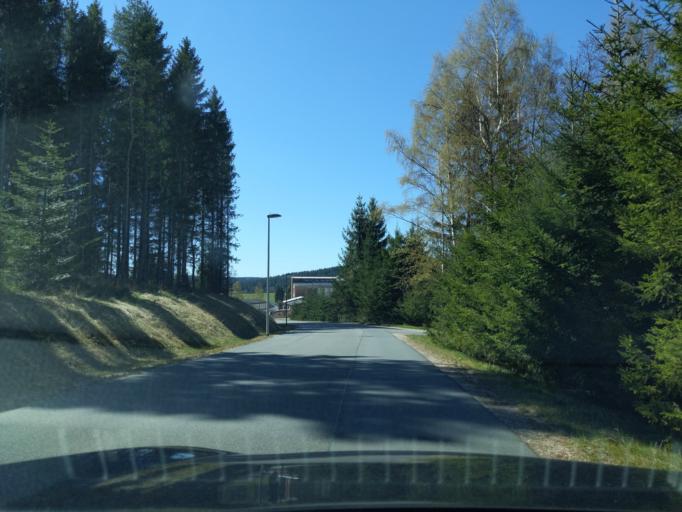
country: DE
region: Saxony
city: Stutzengrun
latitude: 50.5224
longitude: 12.5340
